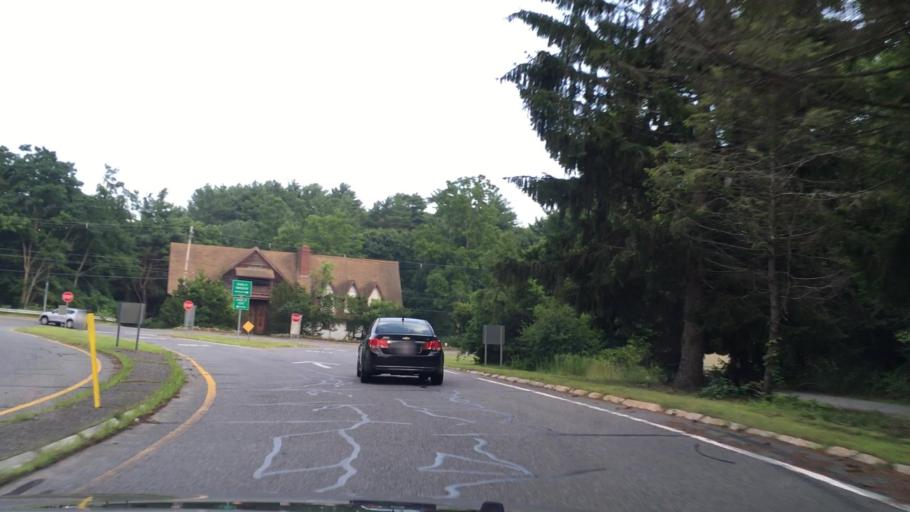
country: US
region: Massachusetts
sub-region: Essex County
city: Essex
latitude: 42.5891
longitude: -70.7667
